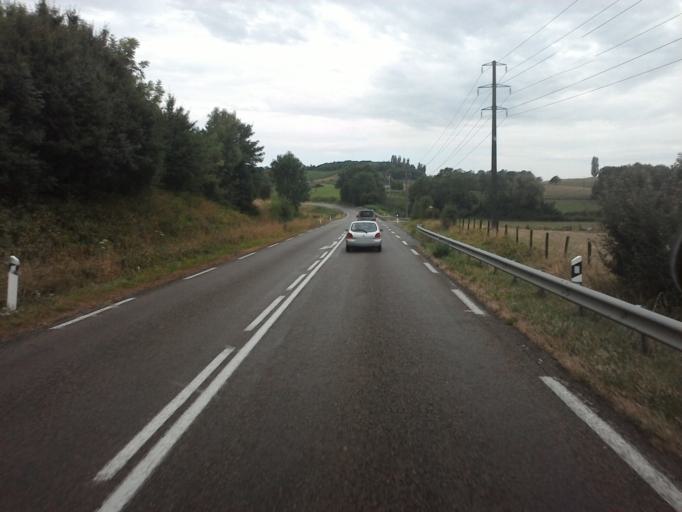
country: FR
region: Franche-Comte
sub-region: Departement du Jura
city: Arbois
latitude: 46.8954
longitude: 5.7350
